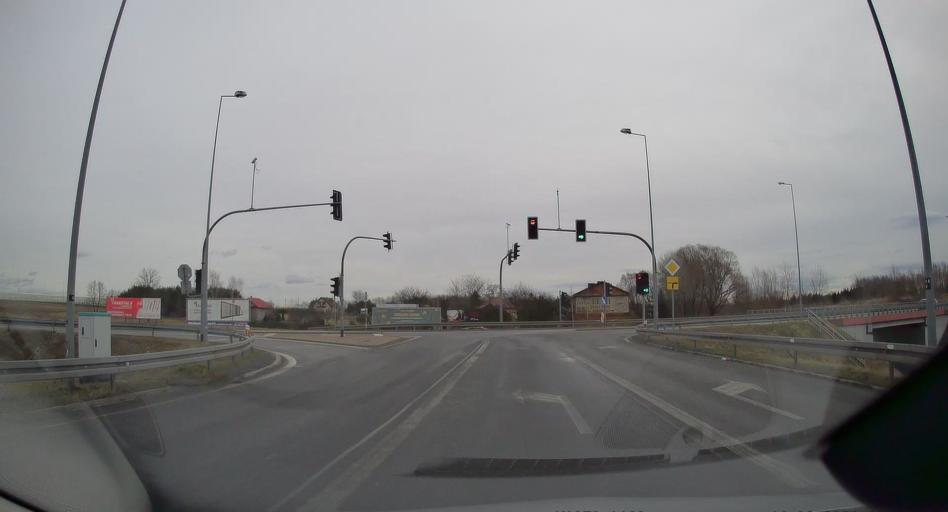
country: PL
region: Lesser Poland Voivodeship
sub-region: Powiat wielicki
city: Targowisko
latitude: 49.9873
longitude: 20.2820
